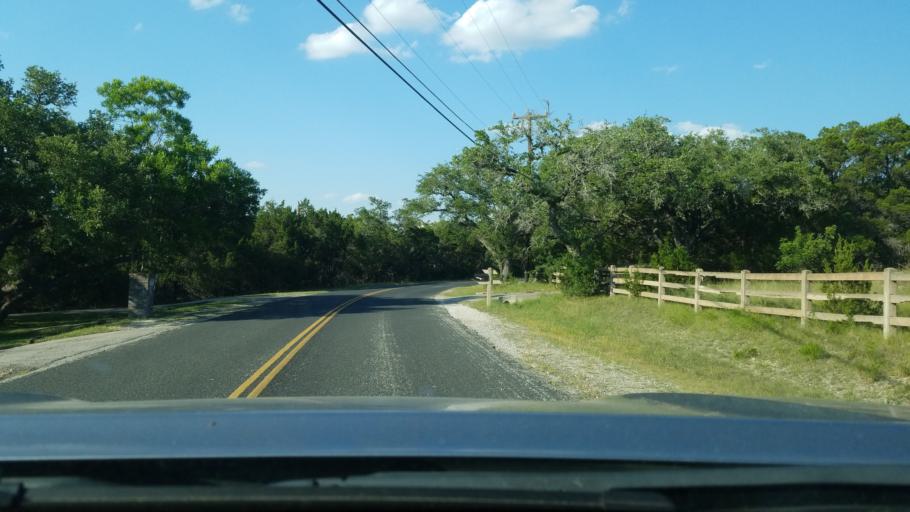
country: US
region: Texas
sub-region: Comal County
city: Bulverde
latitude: 29.7121
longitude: -98.4419
